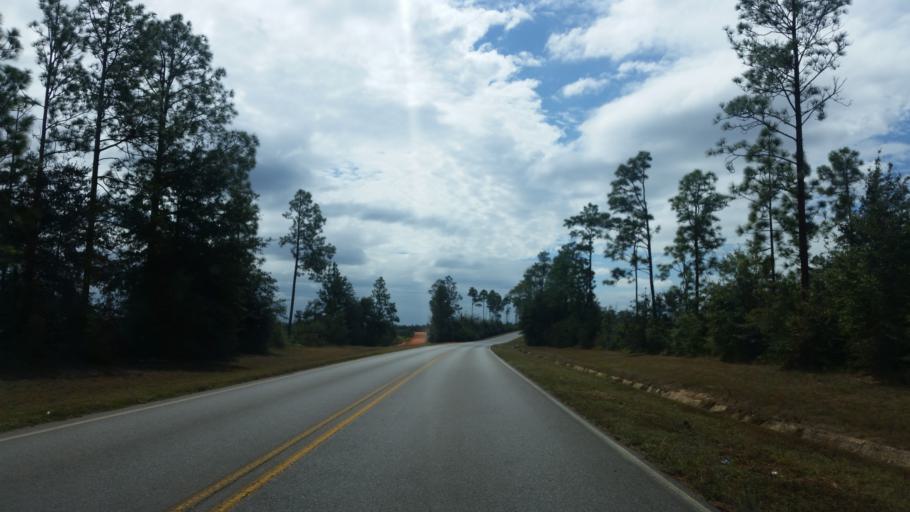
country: US
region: Florida
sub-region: Santa Rosa County
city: Point Baker
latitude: 30.7305
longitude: -86.9520
